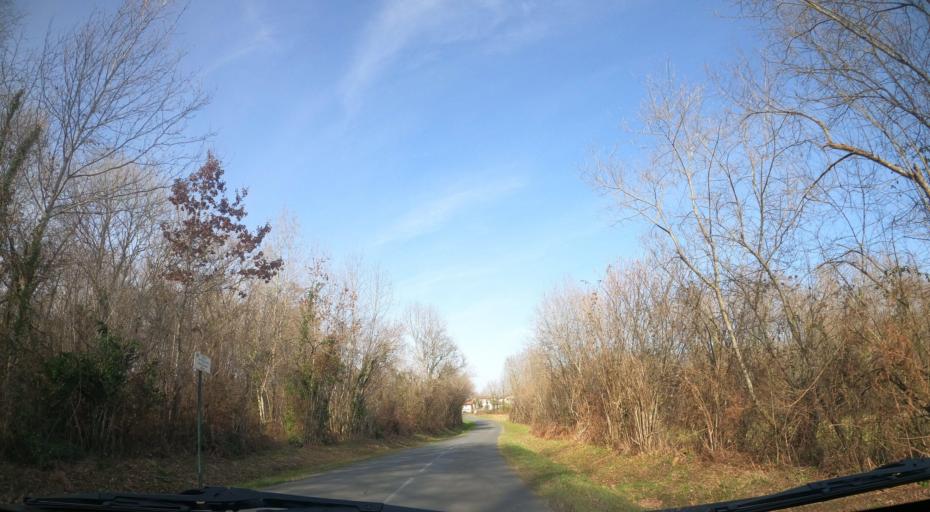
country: FR
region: Aquitaine
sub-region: Departement des Pyrenees-Atlantiques
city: Briscous
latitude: 43.4433
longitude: -1.3701
